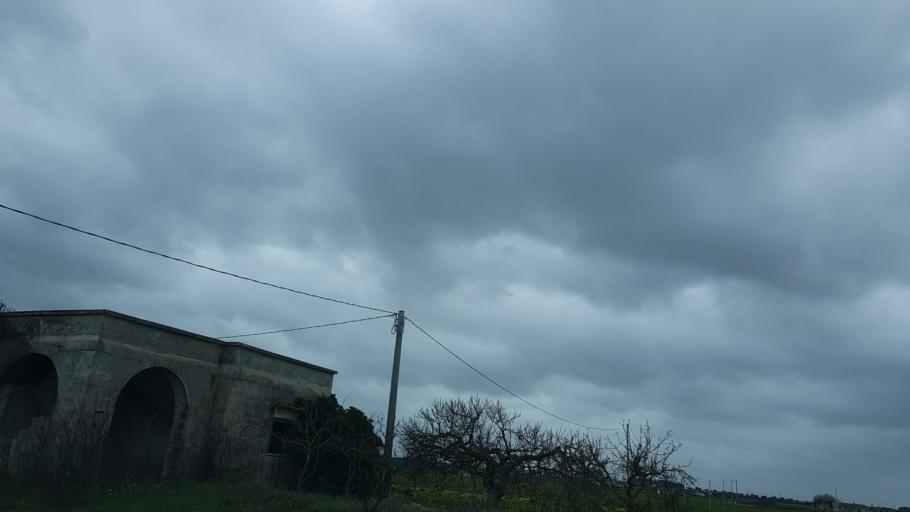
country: IT
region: Apulia
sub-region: Provincia di Brindisi
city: Brindisi
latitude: 40.6637
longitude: 17.8646
